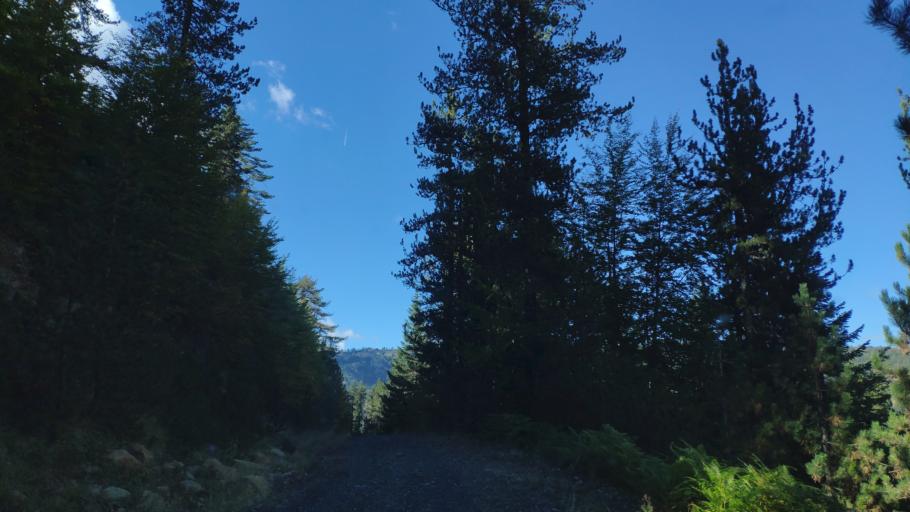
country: GR
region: Epirus
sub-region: Nomos Ioanninon
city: Metsovo
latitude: 39.8917
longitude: 21.2091
